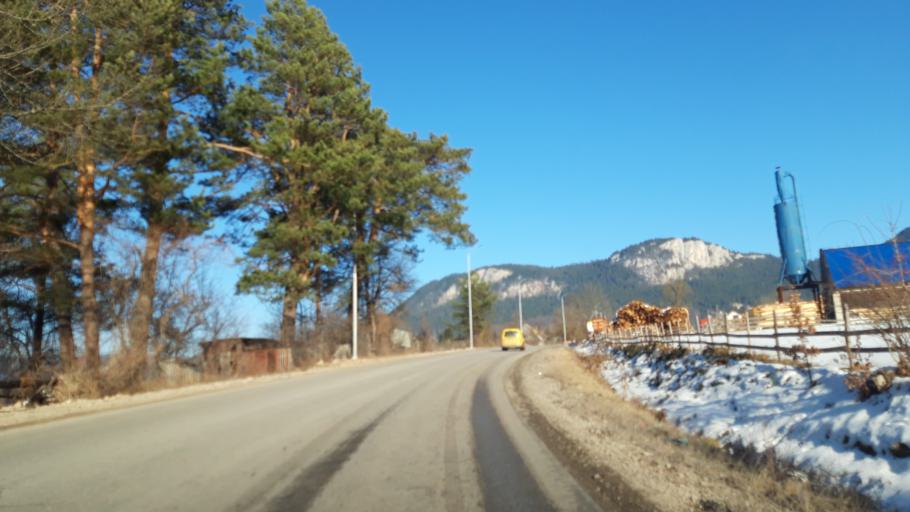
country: BA
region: Republika Srpska
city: Pale
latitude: 43.8912
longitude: 18.6197
